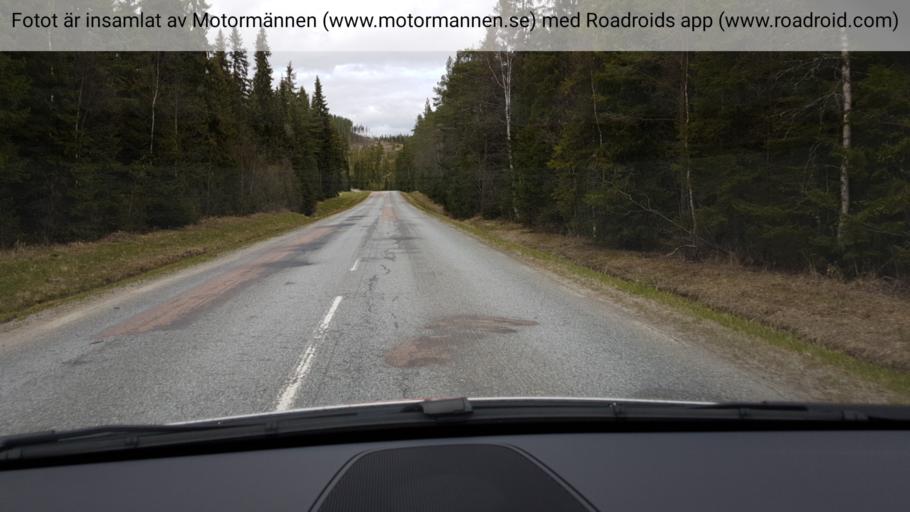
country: SE
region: Jaemtland
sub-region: Braecke Kommun
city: Braecke
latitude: 62.7845
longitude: 15.4750
